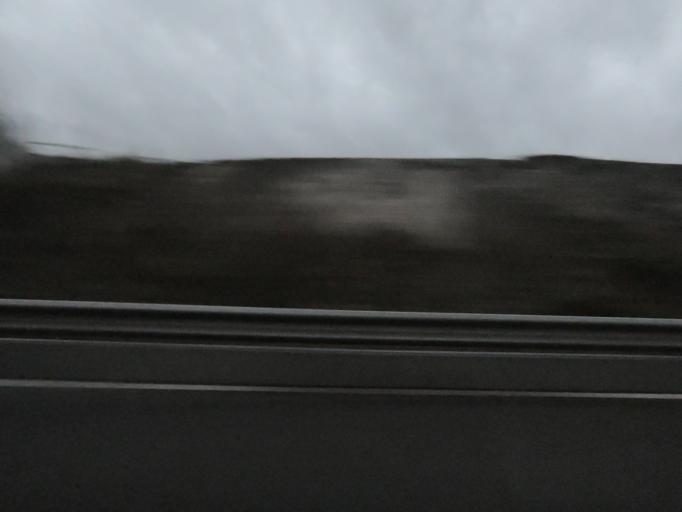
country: PT
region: Setubal
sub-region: Seixal
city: Arrentela
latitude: 38.5942
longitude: -9.1001
